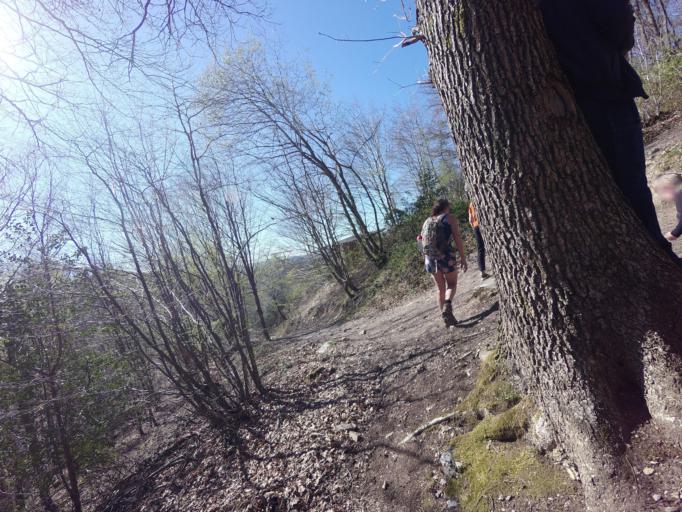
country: BE
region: Wallonia
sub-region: Province de Liege
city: Trois-Ponts
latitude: 50.3952
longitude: 5.8843
